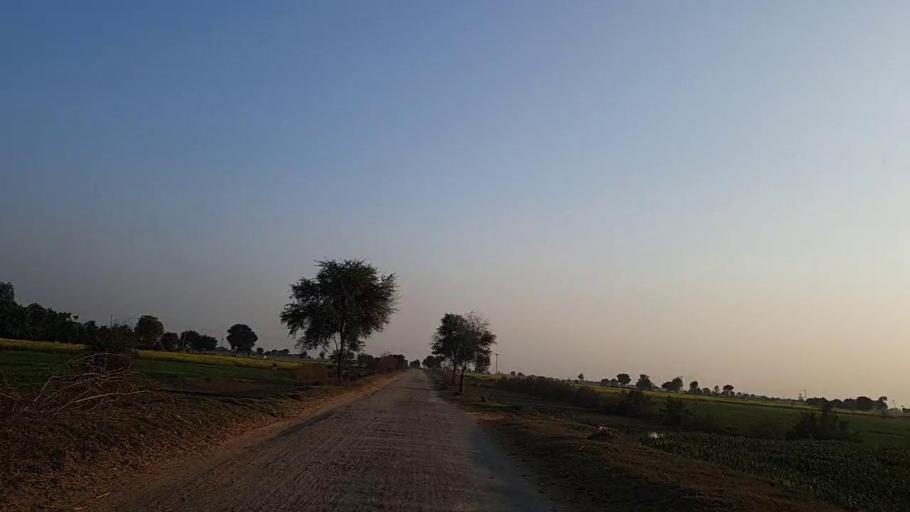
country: PK
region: Sindh
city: Shahdadpur
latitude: 26.0144
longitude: 68.4903
